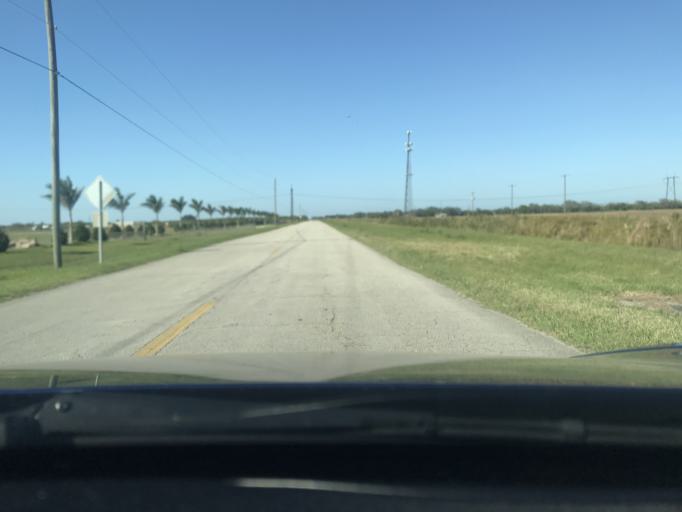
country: US
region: Florida
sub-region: Saint Lucie County
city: Fort Pierce South
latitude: 27.3767
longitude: -80.4976
